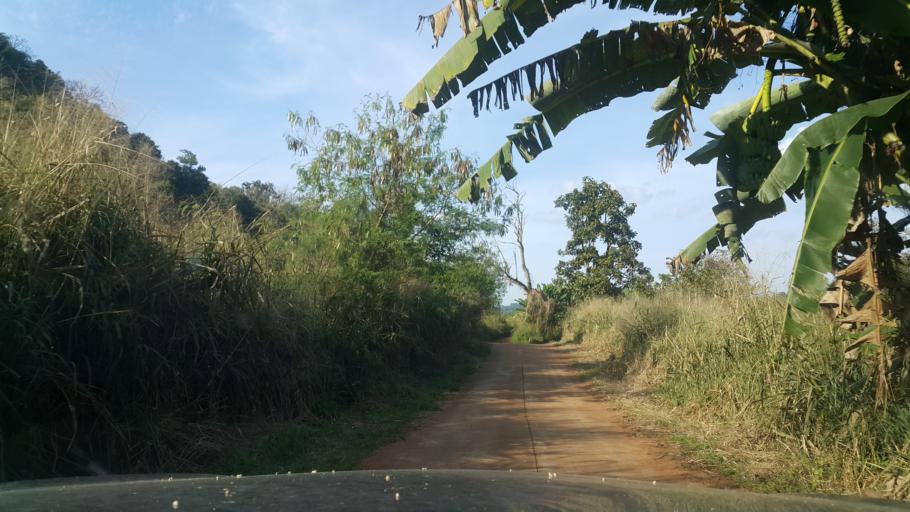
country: TH
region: Chiang Mai
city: Samoeng
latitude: 18.9826
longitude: 98.6834
